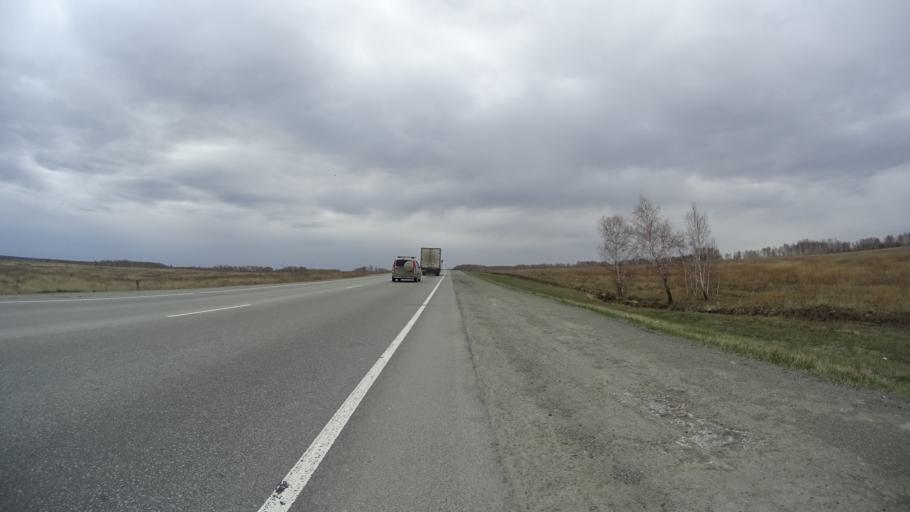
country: RU
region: Chelyabinsk
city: Yemanzhelinsk
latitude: 54.7069
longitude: 61.2572
